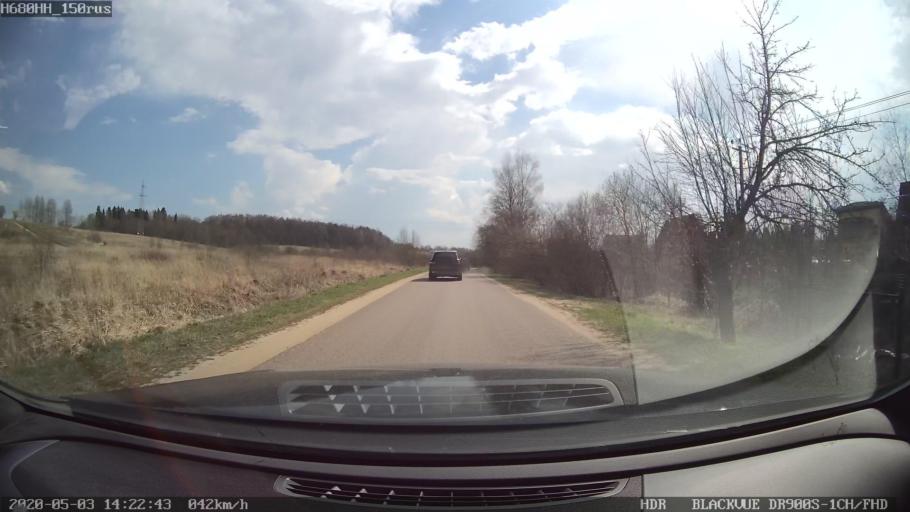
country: RU
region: Moskovskaya
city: Solnechnogorsk
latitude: 56.2574
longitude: 36.9912
